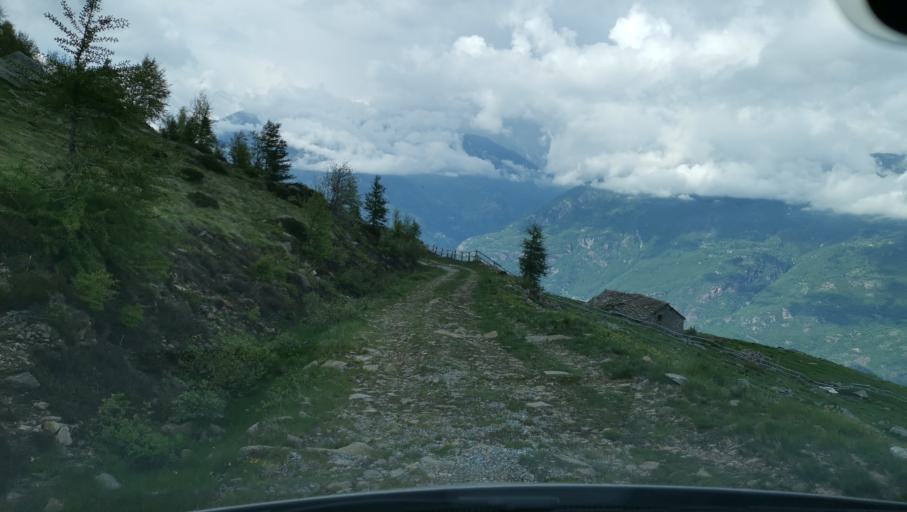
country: IT
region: Piedmont
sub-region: Provincia di Torino
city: Tavagnasco
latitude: 45.5309
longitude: 7.7904
